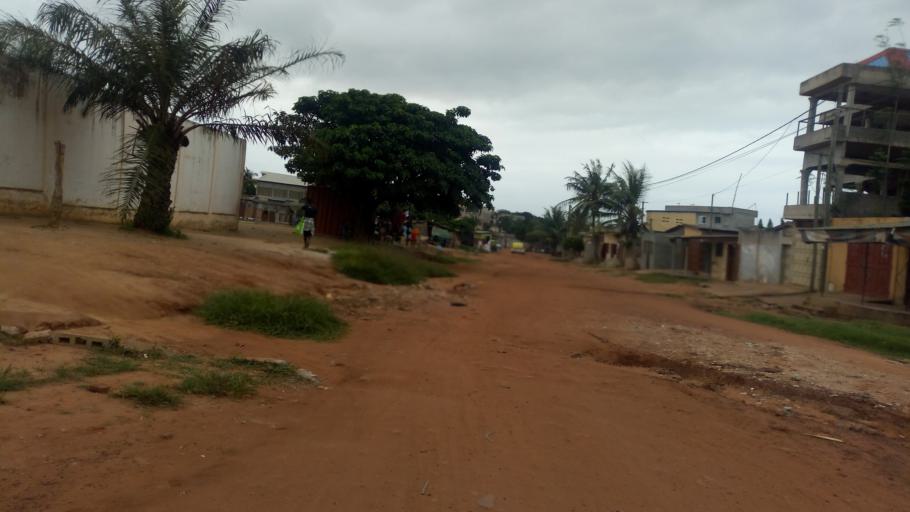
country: TG
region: Maritime
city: Lome
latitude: 6.1732
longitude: 1.1756
